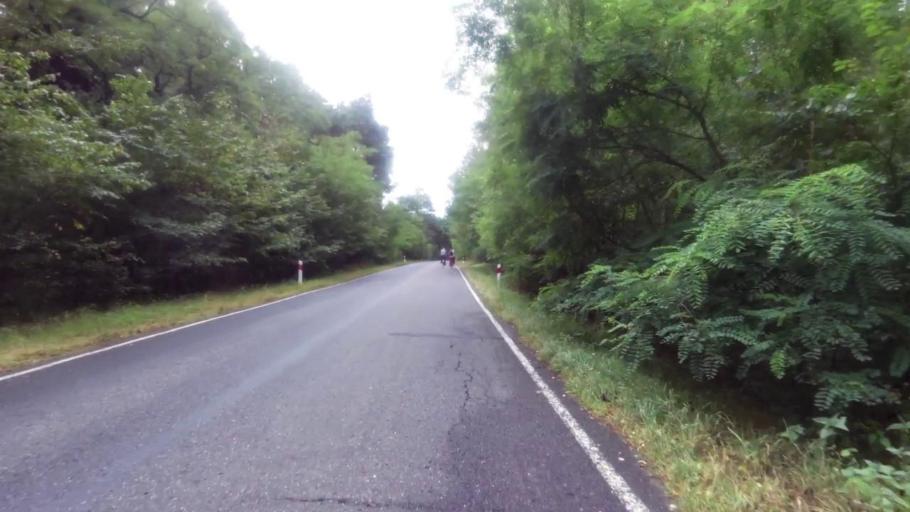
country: PL
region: West Pomeranian Voivodeship
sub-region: Powiat mysliborski
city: Debno
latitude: 52.6939
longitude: 14.6451
